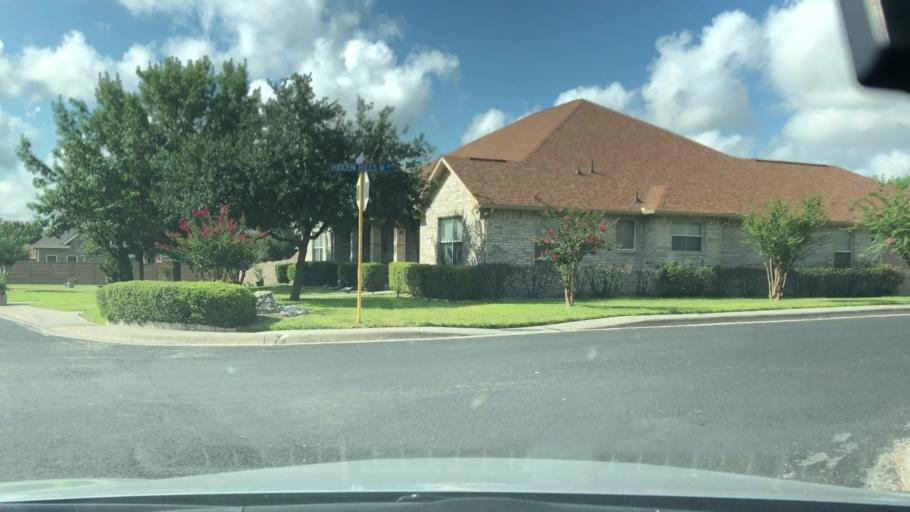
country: US
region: Texas
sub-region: Bexar County
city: Converse
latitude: 29.4874
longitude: -98.3370
